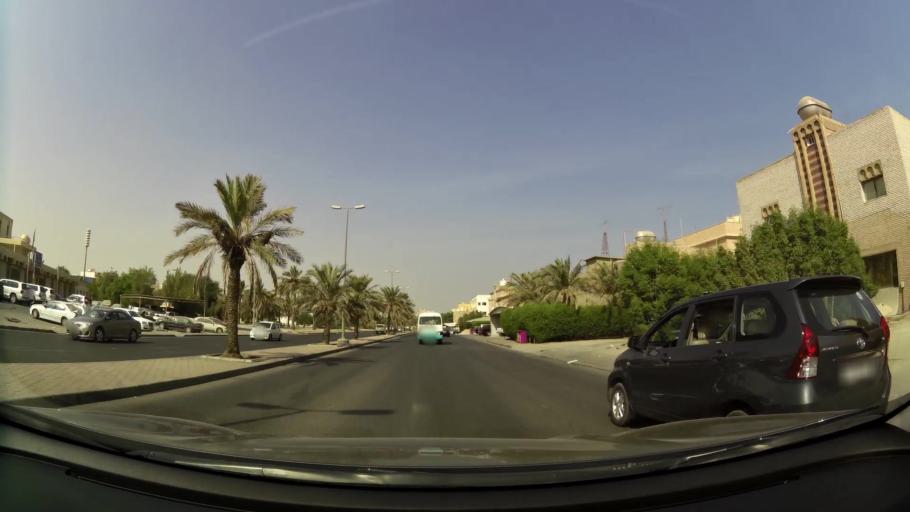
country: KW
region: Al Ahmadi
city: Al Fahahil
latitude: 29.0864
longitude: 48.1227
